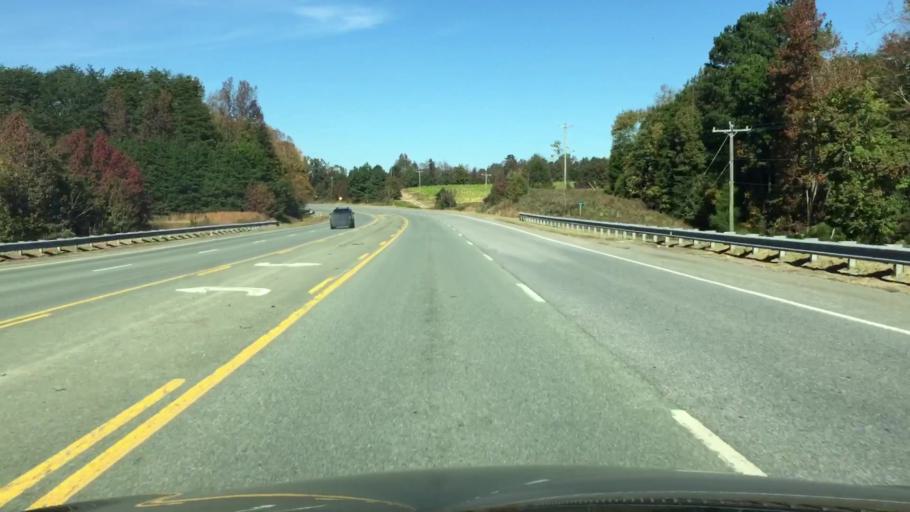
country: US
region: North Carolina
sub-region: Rockingham County
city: Reidsville
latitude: 36.3187
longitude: -79.6330
